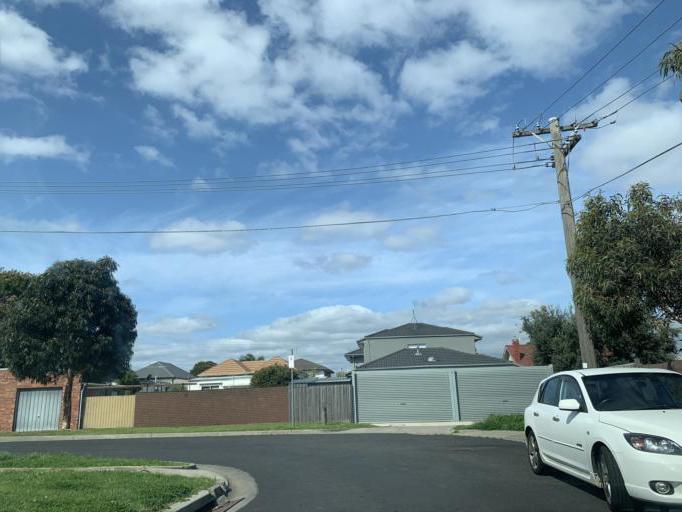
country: AU
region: Victoria
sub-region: Moreland
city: Coburg
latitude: -37.7441
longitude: 144.9705
